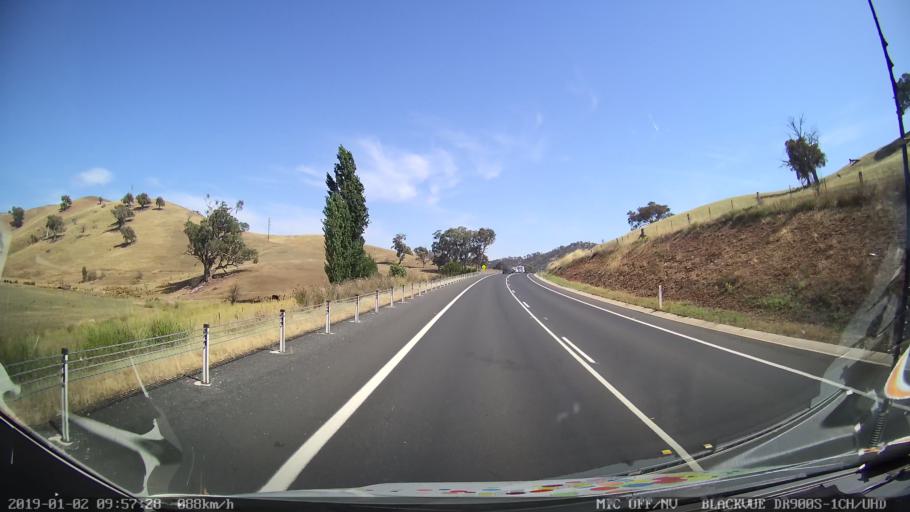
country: AU
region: New South Wales
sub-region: Tumut Shire
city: Tumut
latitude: -35.2051
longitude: 148.1659
